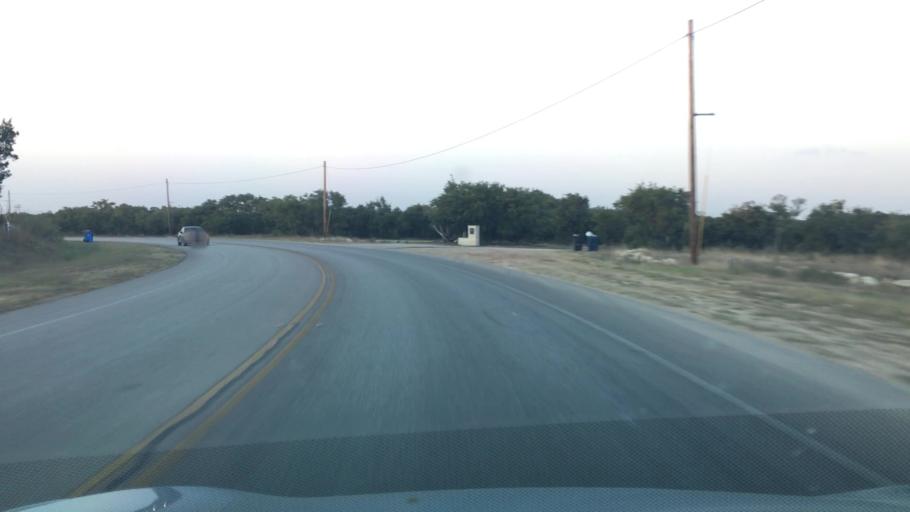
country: US
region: Texas
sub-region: Hays County
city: Dripping Springs
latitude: 30.1920
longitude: -97.9975
